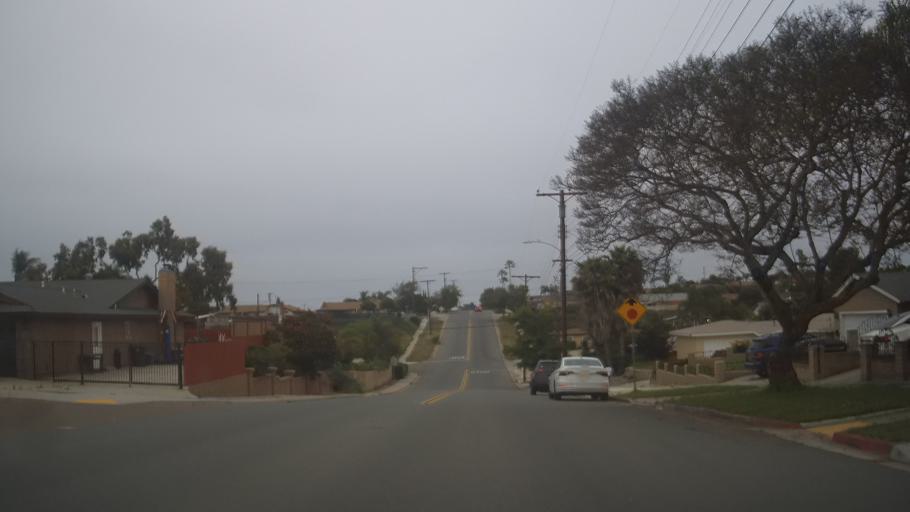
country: US
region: California
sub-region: San Diego County
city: Bonita
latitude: 32.6221
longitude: -117.0475
